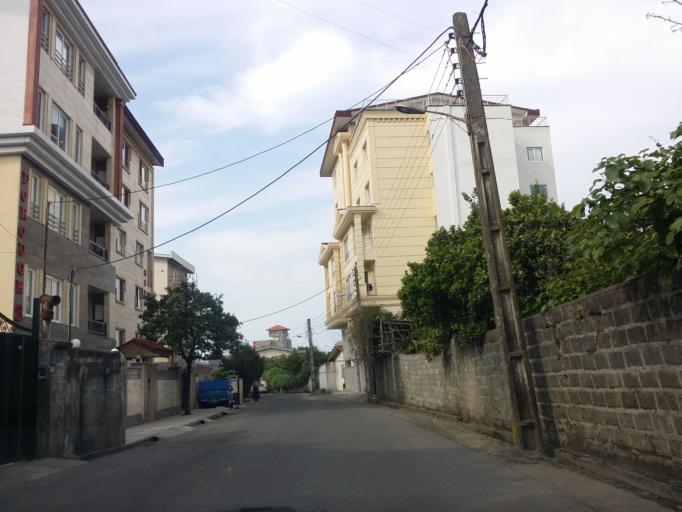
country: IR
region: Mazandaran
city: Chalus
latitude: 36.6548
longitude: 51.4136
